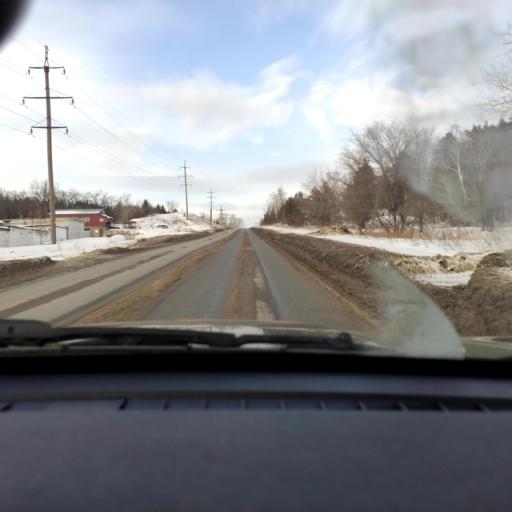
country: RU
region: Samara
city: Pribrezhnyy
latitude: 53.4921
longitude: 49.8475
